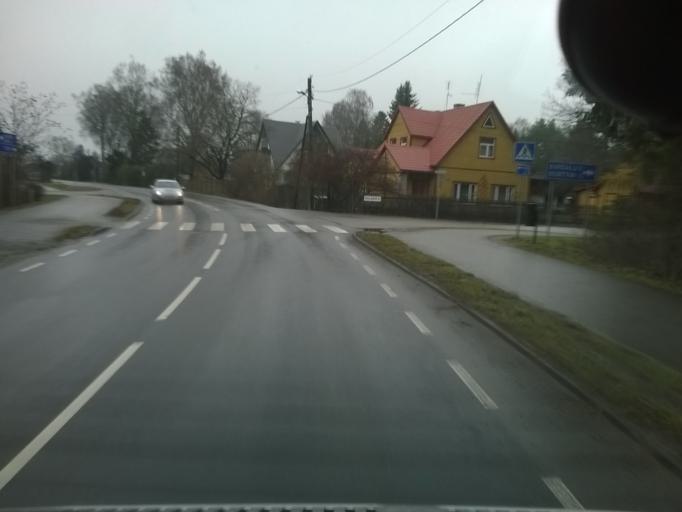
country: EE
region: Harju
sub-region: Saku vald
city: Saku
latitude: 59.2352
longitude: 24.6831
